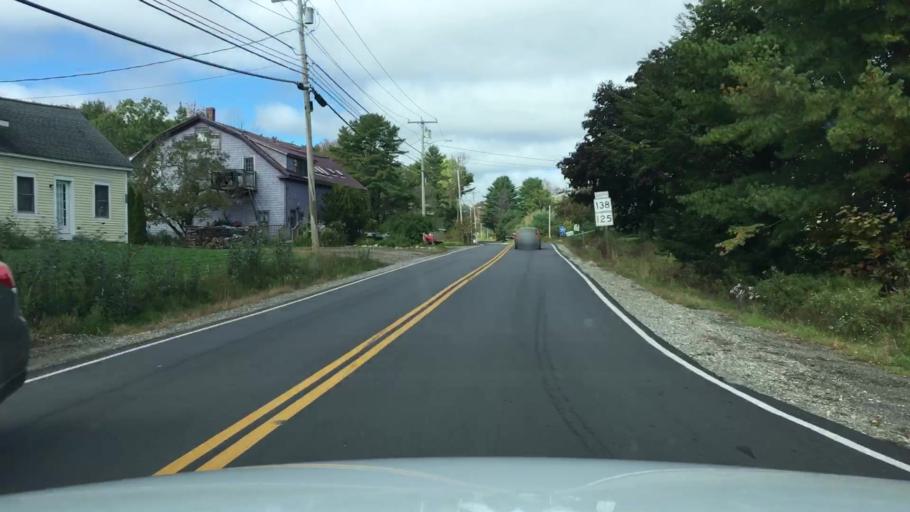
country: US
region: Maine
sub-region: Sagadahoc County
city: Topsham
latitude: 44.0118
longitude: -69.9073
